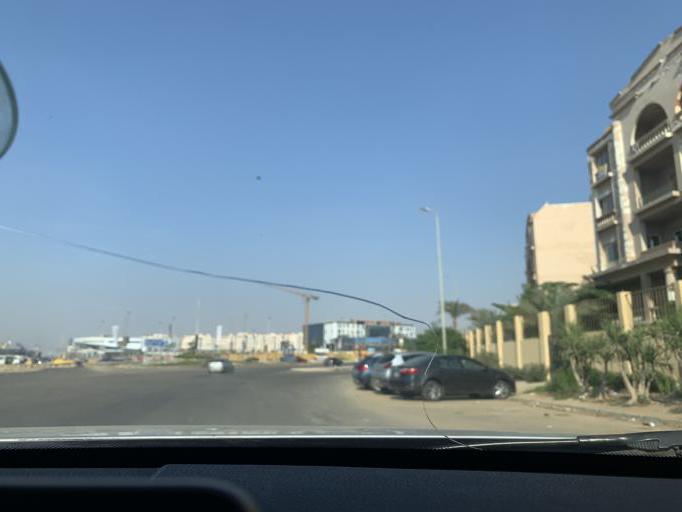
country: EG
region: Muhafazat al Qalyubiyah
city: Al Khankah
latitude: 30.0243
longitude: 31.4752
